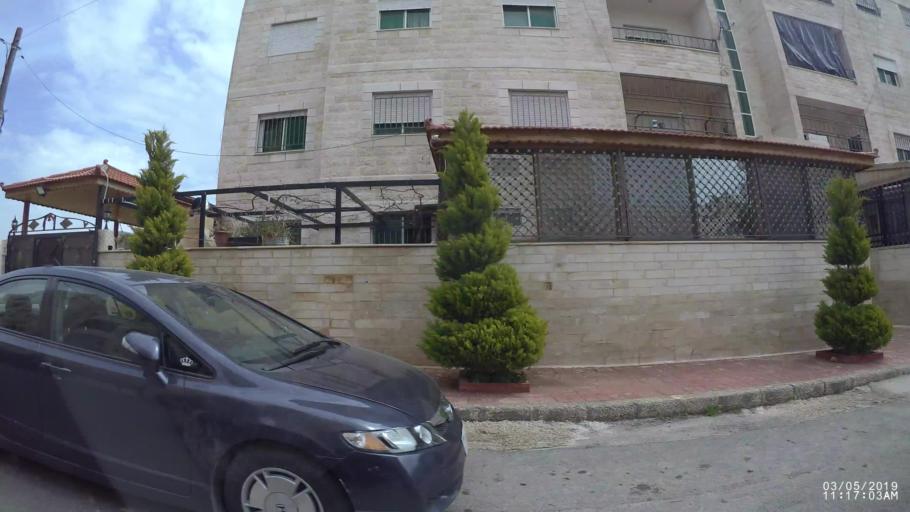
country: JO
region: Amman
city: Amman
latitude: 31.9896
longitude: 35.9272
